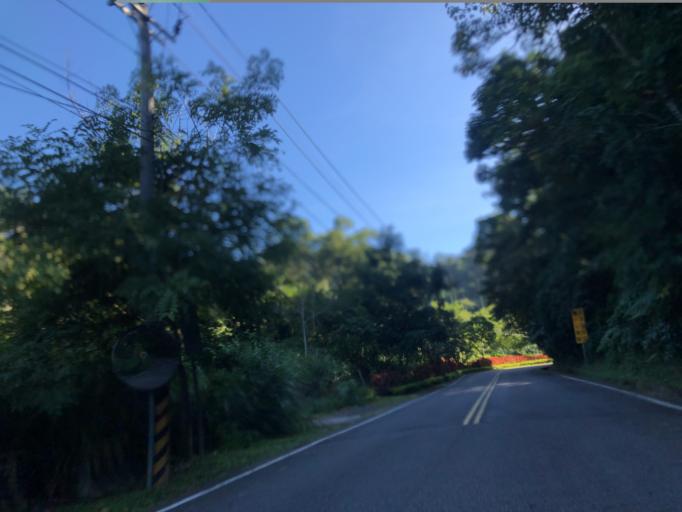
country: TW
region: Taiwan
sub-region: Miaoli
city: Miaoli
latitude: 24.5895
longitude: 120.9226
